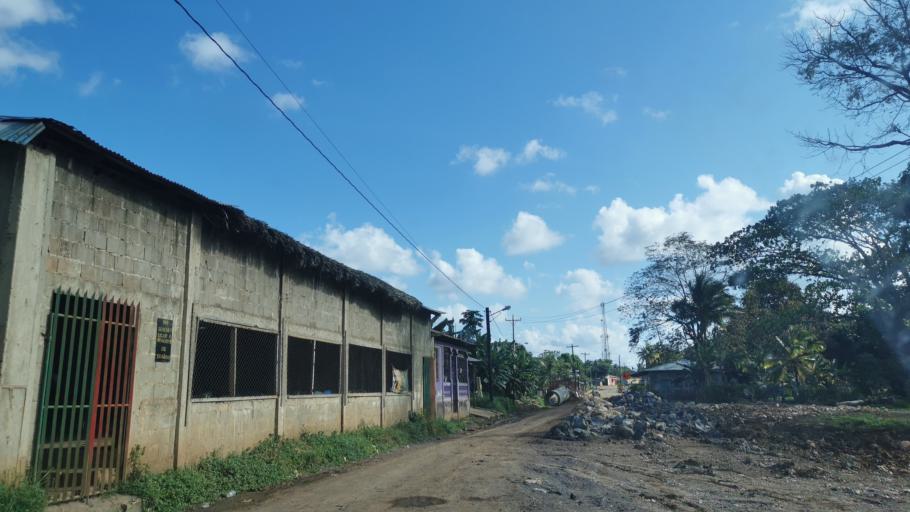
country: NI
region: Atlantico Sur
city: Laguna de Perlas
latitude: 12.2459
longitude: -83.7432
